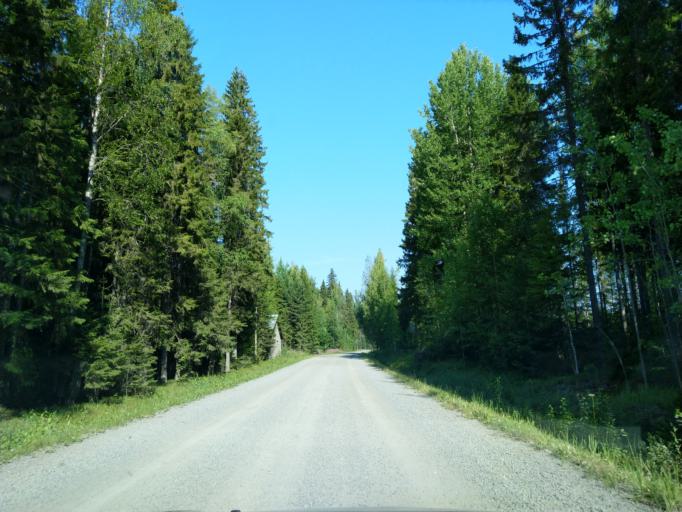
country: FI
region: Satakunta
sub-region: Pori
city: Laengelmaeki
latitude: 61.7324
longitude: 22.1741
